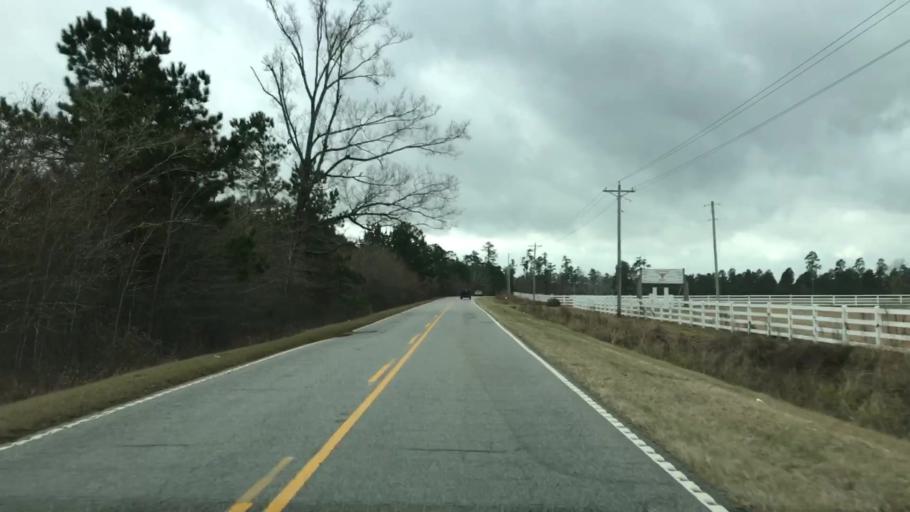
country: US
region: South Carolina
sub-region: Florence County
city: Johnsonville
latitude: 33.6519
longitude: -79.4194
